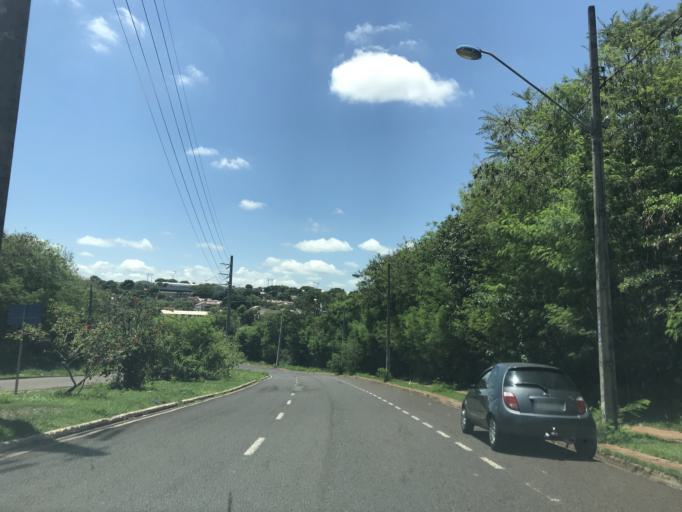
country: BR
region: Parana
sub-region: Maringa
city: Maringa
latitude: -23.4537
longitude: -51.9316
